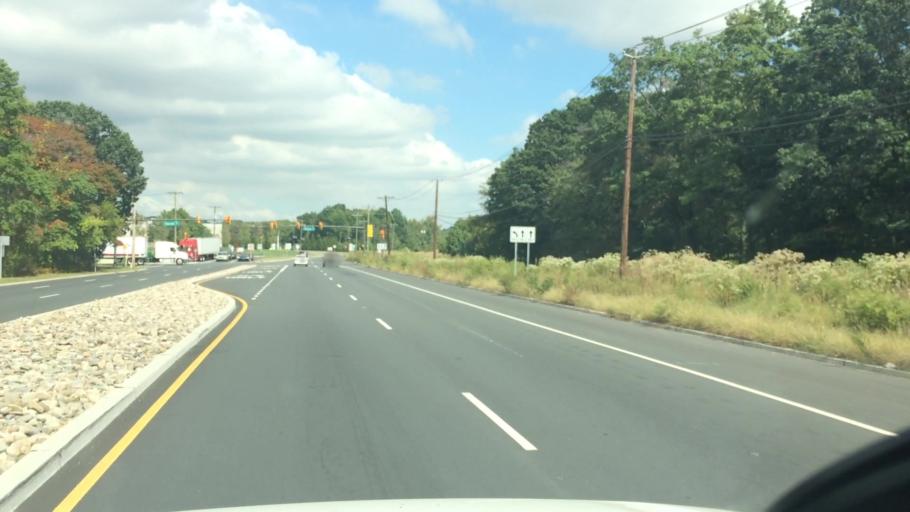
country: US
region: New Jersey
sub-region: Middlesex County
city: Fords
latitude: 40.5132
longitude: -74.3295
